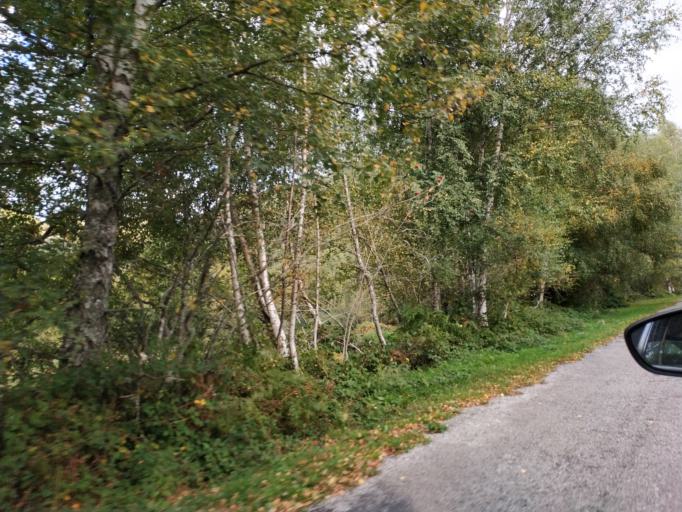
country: ES
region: Castille and Leon
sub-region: Provincia de Leon
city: Candin
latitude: 42.8637
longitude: -6.8577
